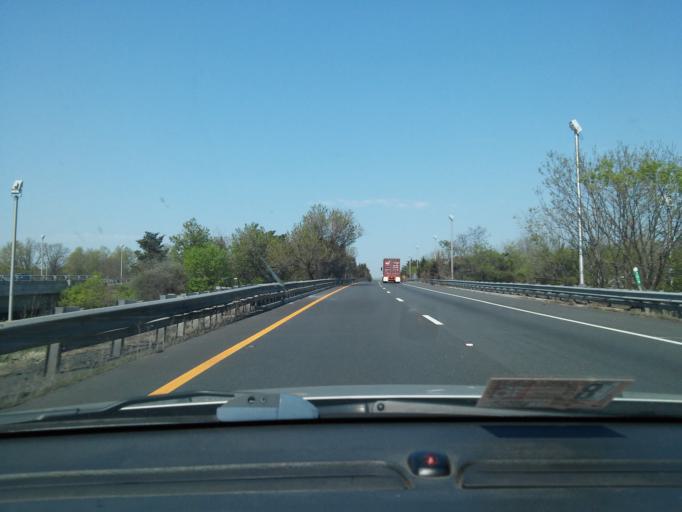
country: US
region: New Jersey
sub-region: Somerset County
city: Bedminster
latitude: 40.6428
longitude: -74.6444
